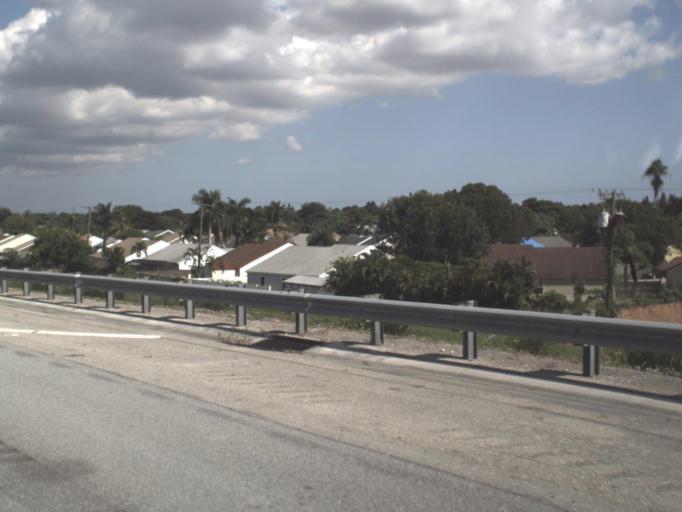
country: US
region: Florida
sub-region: Palm Beach County
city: Greenacres City
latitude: 26.5919
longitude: -80.1733
